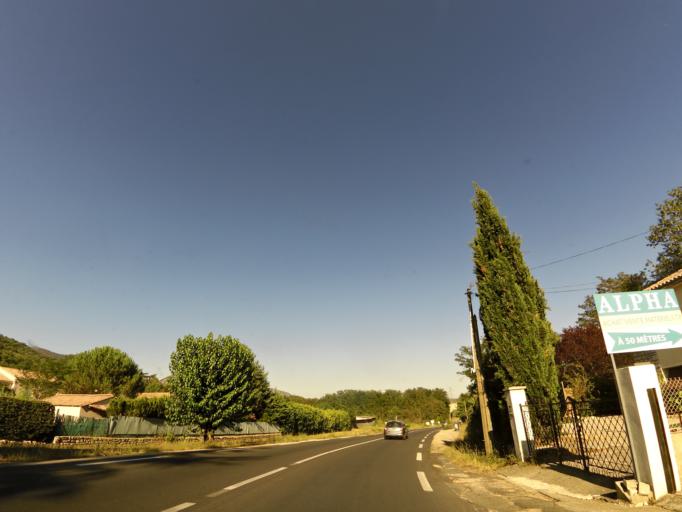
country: FR
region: Languedoc-Roussillon
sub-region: Departement de l'Herault
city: Ganges
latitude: 43.9443
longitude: 3.7185
